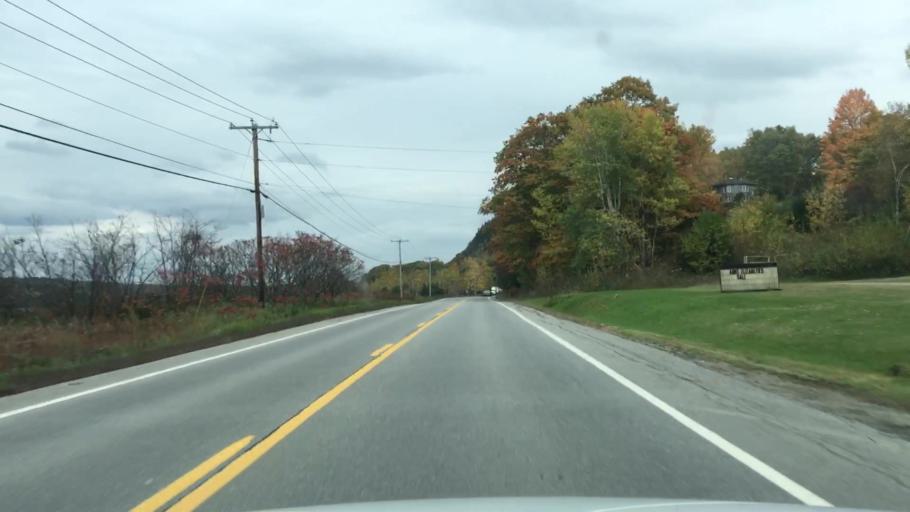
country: US
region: Maine
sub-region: Waldo County
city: Frankfort
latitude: 44.5948
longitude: -68.8656
